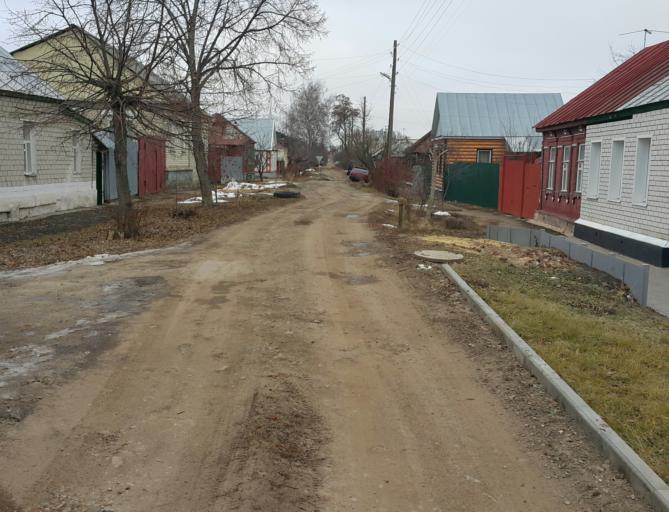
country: RU
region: Tambov
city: Tambov
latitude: 52.7267
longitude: 41.4015
